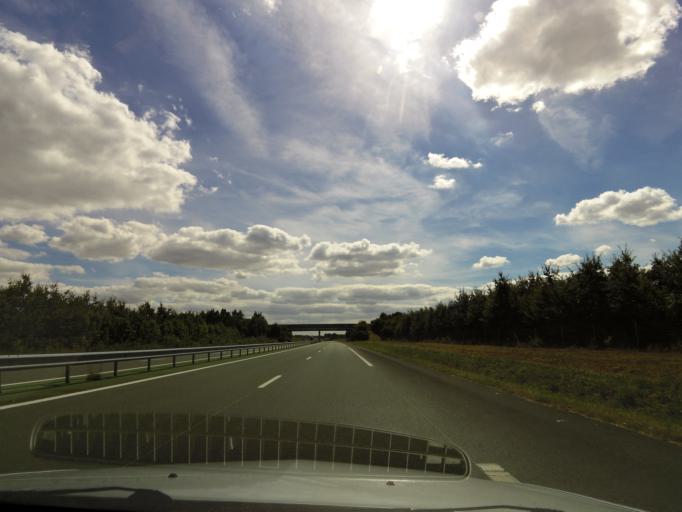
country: FR
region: Pays de la Loire
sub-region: Departement de la Vendee
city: La Ferriere
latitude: 46.7308
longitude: -1.2754
